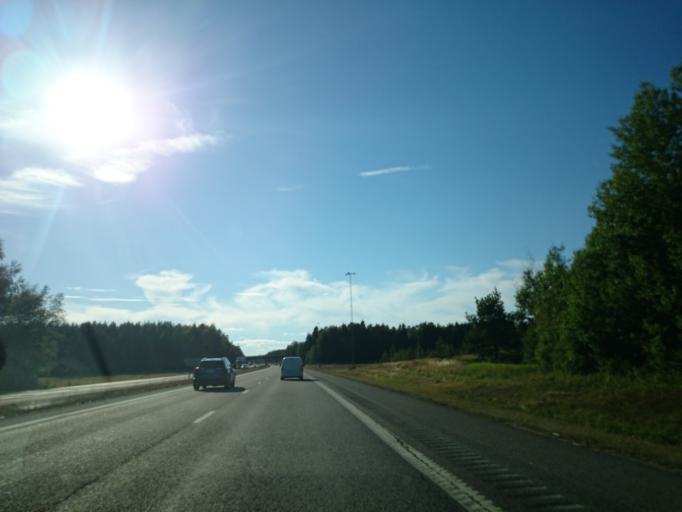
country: SE
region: Soedermanland
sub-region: Nykopings Kommun
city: Svalsta
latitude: 58.7492
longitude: 16.9196
